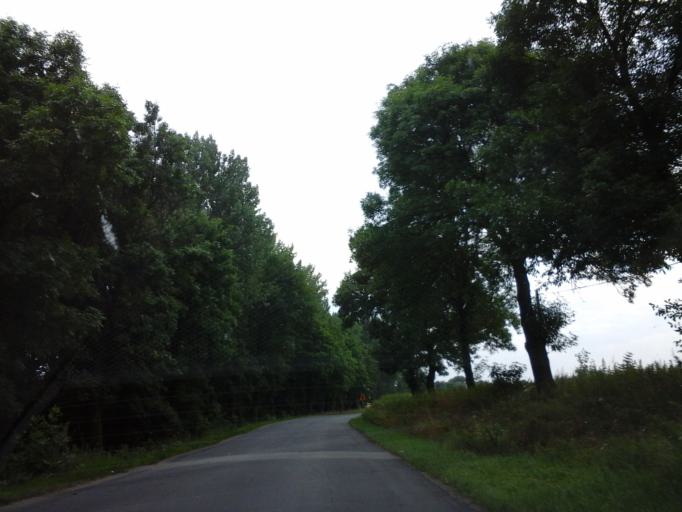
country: PL
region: Lower Silesian Voivodeship
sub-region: Powiat zabkowicki
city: Zabkowice Slaskie
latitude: 50.6075
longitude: 16.8359
